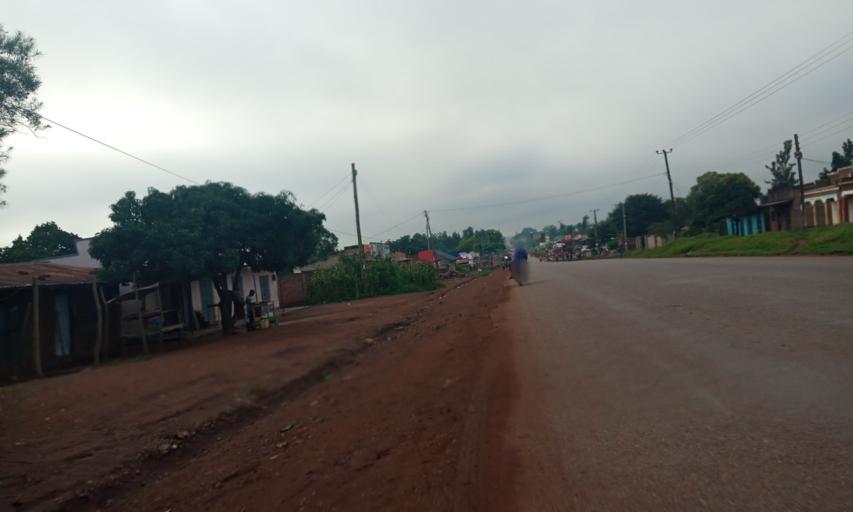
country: UG
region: Eastern Region
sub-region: Mbale District
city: Mbale
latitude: 1.1147
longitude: 34.1710
